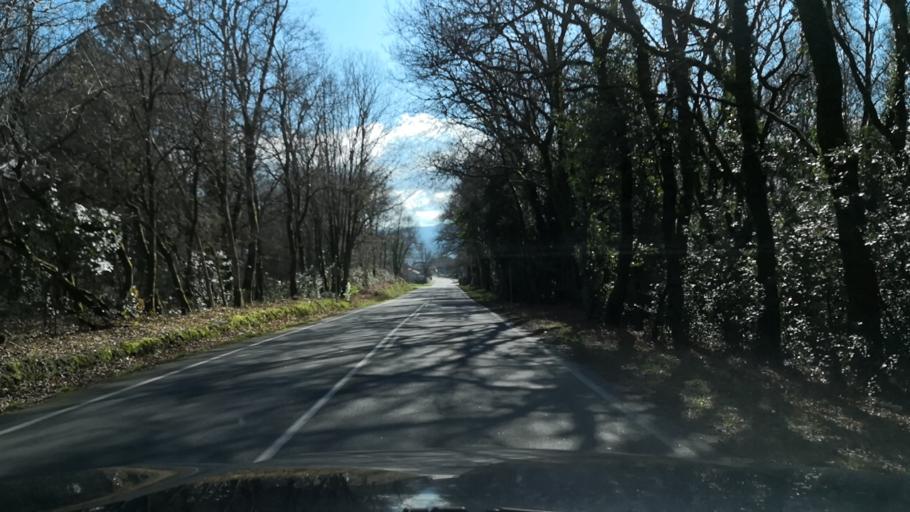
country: ES
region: Galicia
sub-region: Provincia da Coruna
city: Ribeira
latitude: 42.7158
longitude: -8.4446
